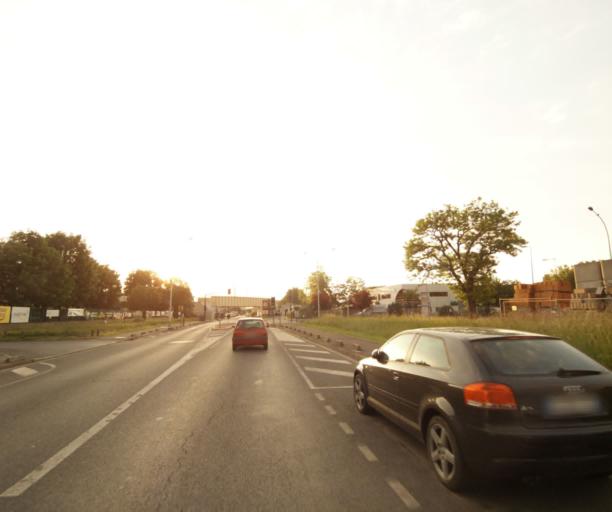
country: FR
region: Ile-de-France
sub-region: Departement des Hauts-de-Seine
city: Villeneuve-la-Garenne
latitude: 48.9286
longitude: 2.3114
